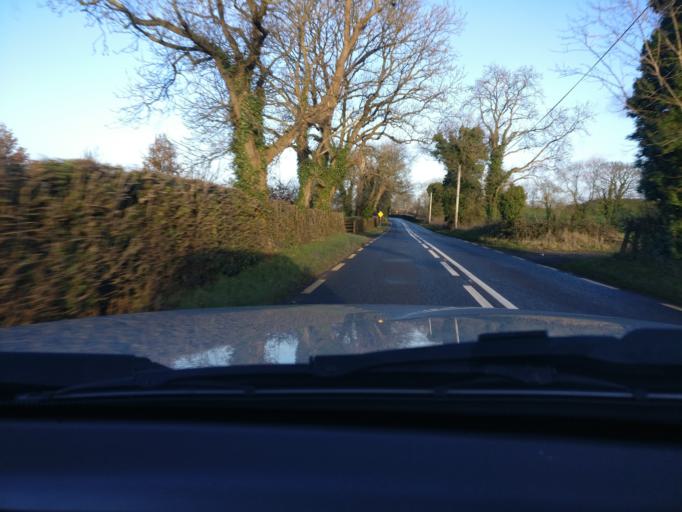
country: IE
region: Ulster
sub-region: An Cabhan
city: Kingscourt
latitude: 53.7933
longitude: -6.7205
